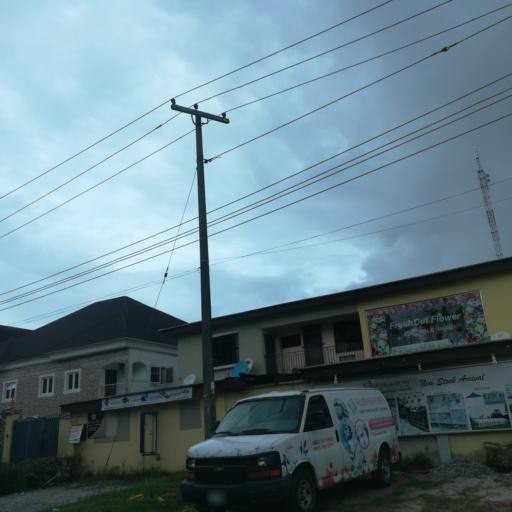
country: NG
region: Lagos
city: Ikoyi
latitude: 6.4381
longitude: 3.4641
